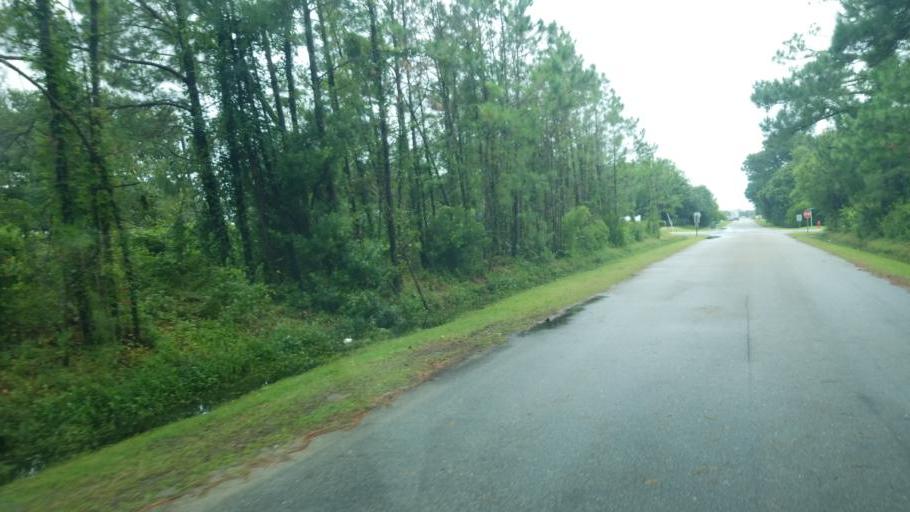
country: US
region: North Carolina
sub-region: Dare County
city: Nags Head
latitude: 35.9886
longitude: -75.6448
